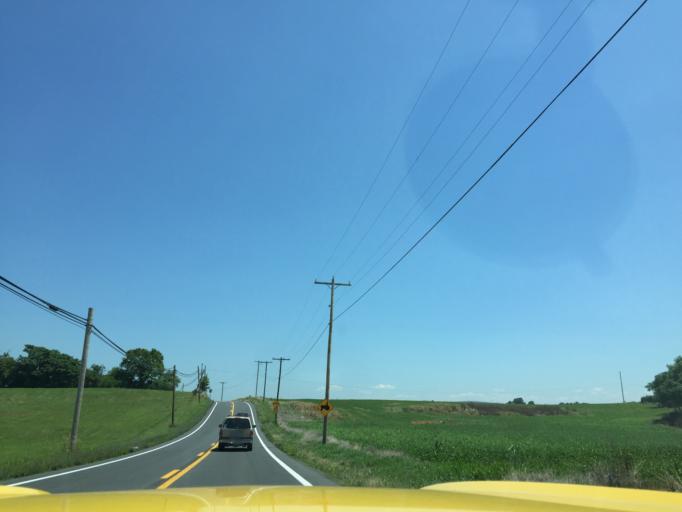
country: US
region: West Virginia
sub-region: Jefferson County
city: Ranson
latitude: 39.2906
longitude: -77.8875
